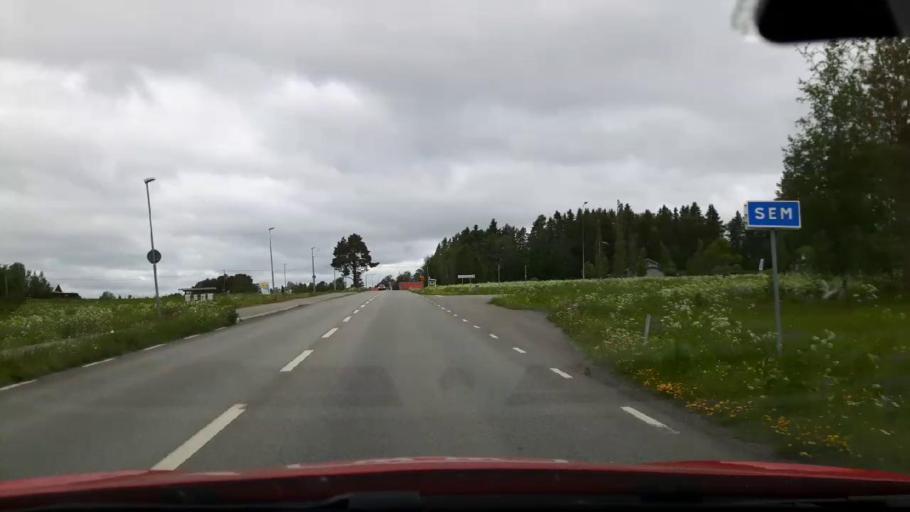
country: SE
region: Jaemtland
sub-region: OEstersunds Kommun
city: Ostersund
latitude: 63.2294
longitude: 14.5867
